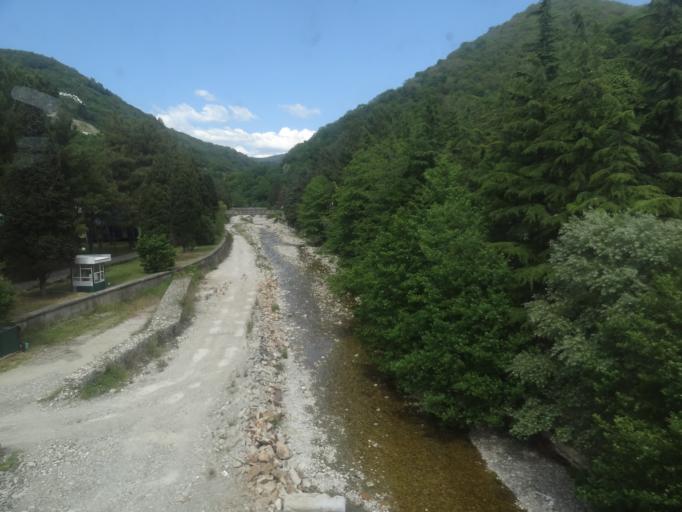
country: RU
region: Krasnodarskiy
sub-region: Sochi City
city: Lazarevskoye
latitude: 43.9399
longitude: 39.2981
